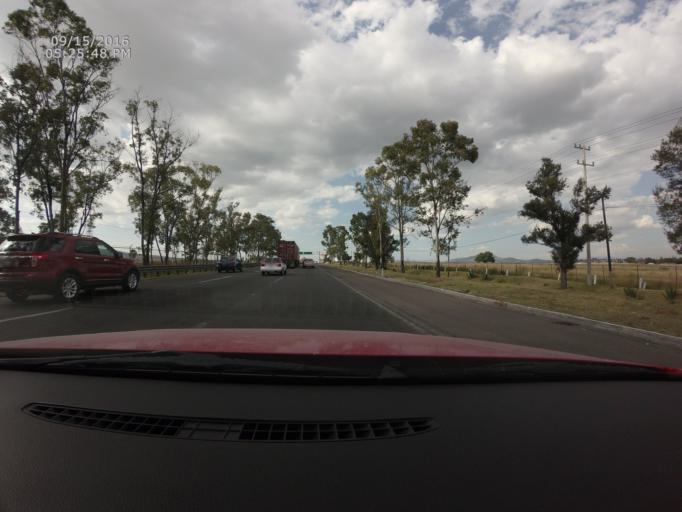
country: MX
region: Mexico
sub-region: Cuautitlan
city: San Jose del Puente
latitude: 19.7325
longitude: -99.2103
